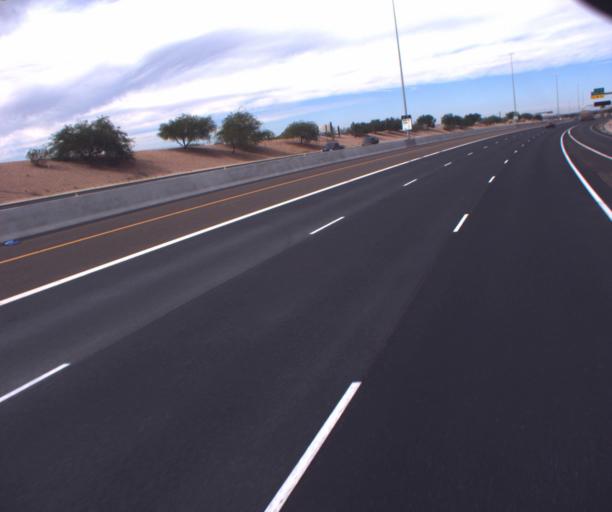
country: US
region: Arizona
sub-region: Maricopa County
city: Mesa
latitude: 33.4767
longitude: -111.7074
